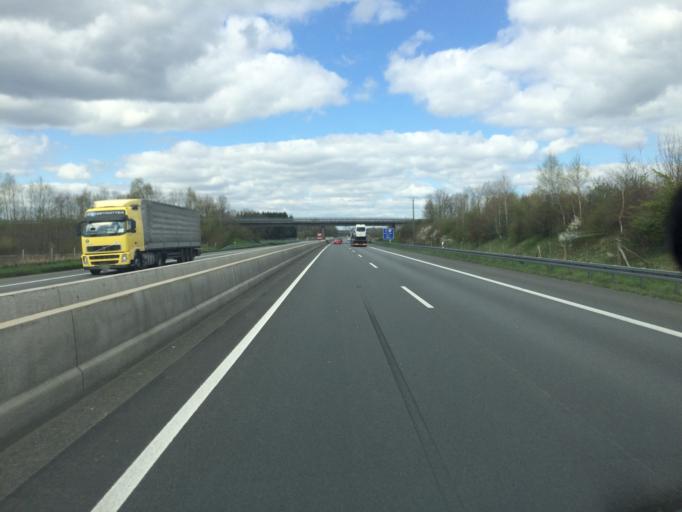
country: DE
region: North Rhine-Westphalia
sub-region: Regierungsbezirk Munster
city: Gescher
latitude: 51.9888
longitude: 7.0500
